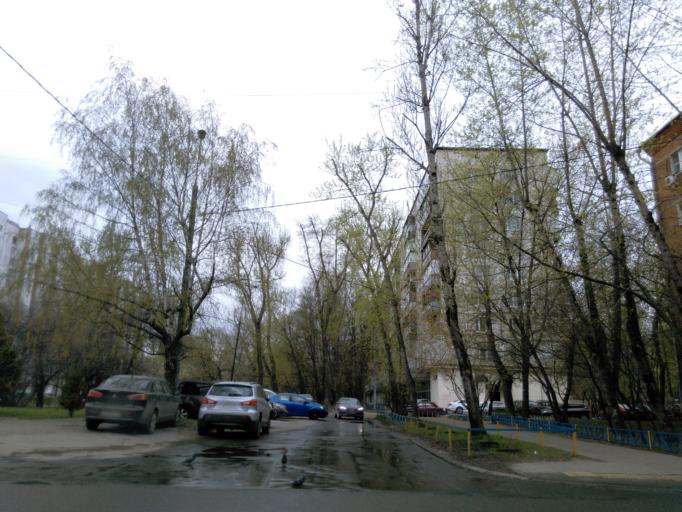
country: RU
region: Moskovskaya
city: Levoberezhnyy
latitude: 55.8475
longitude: 37.4531
